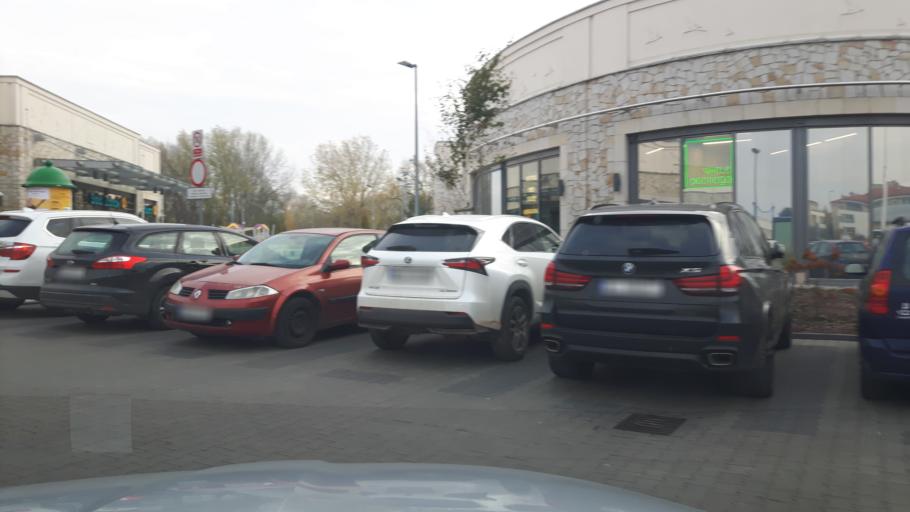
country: PL
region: Masovian Voivodeship
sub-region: Warszawa
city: Wilanow
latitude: 52.1655
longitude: 21.1100
